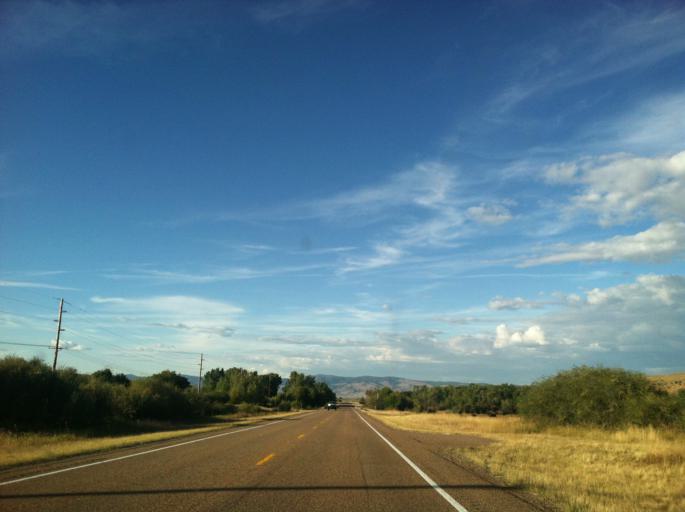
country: US
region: Montana
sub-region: Granite County
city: Philipsburg
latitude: 46.5277
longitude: -113.2242
